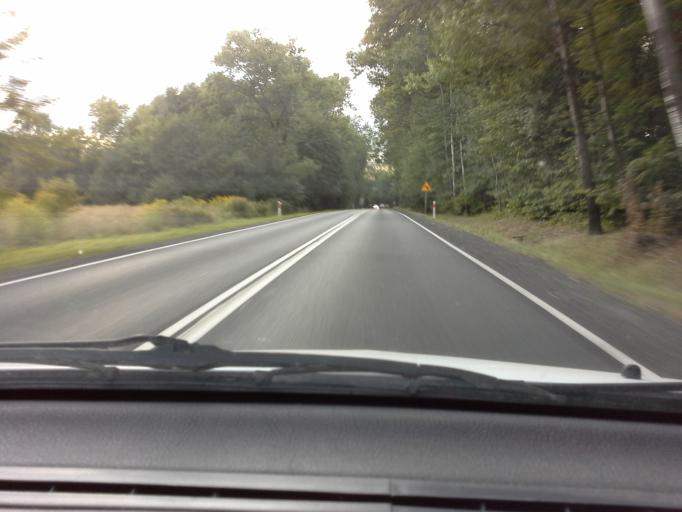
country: PL
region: Lesser Poland Voivodeship
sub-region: Powiat krakowski
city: Filipowice
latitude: 50.1411
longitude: 19.5513
